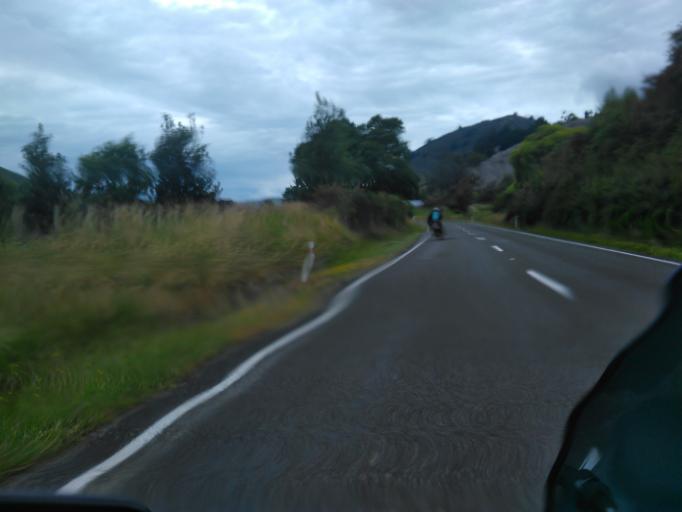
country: NZ
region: Gisborne
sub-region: Gisborne District
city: Gisborne
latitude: -38.4399
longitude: 177.5857
